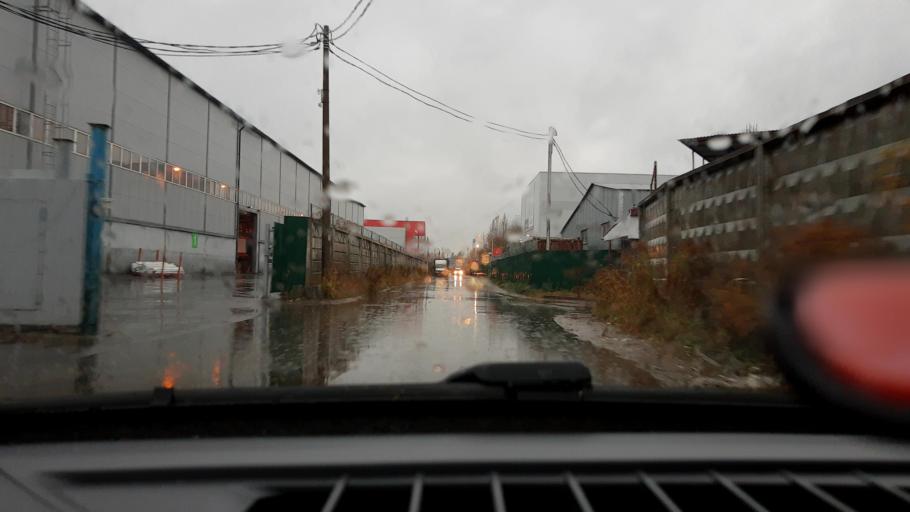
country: RU
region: Nizjnij Novgorod
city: Gorbatovka
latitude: 56.3193
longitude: 43.8526
